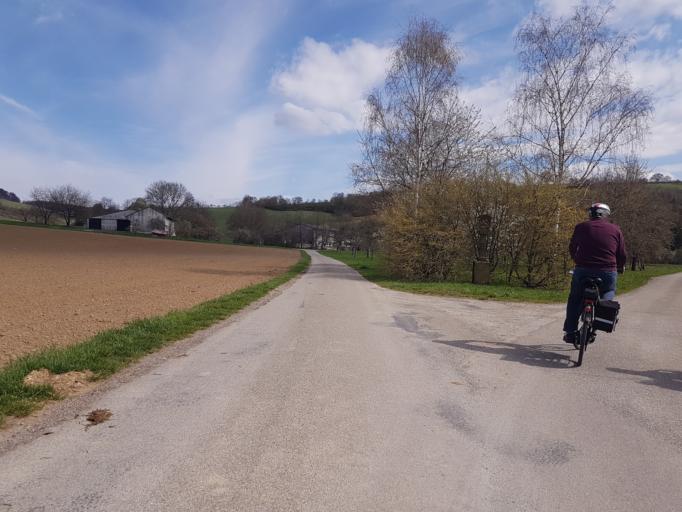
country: DE
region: Baden-Wuerttemberg
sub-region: Regierungsbezirk Stuttgart
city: Krautheim
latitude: 49.3587
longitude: 9.6112
